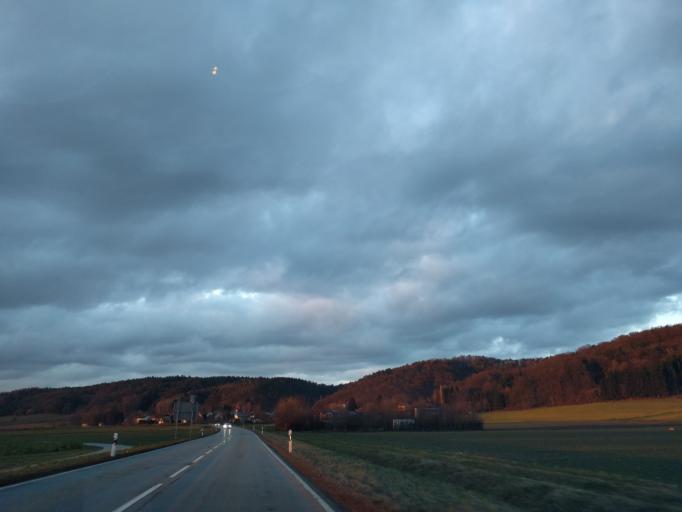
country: DE
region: Bavaria
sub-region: Lower Bavaria
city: Winzer
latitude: 48.7093
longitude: 13.1063
